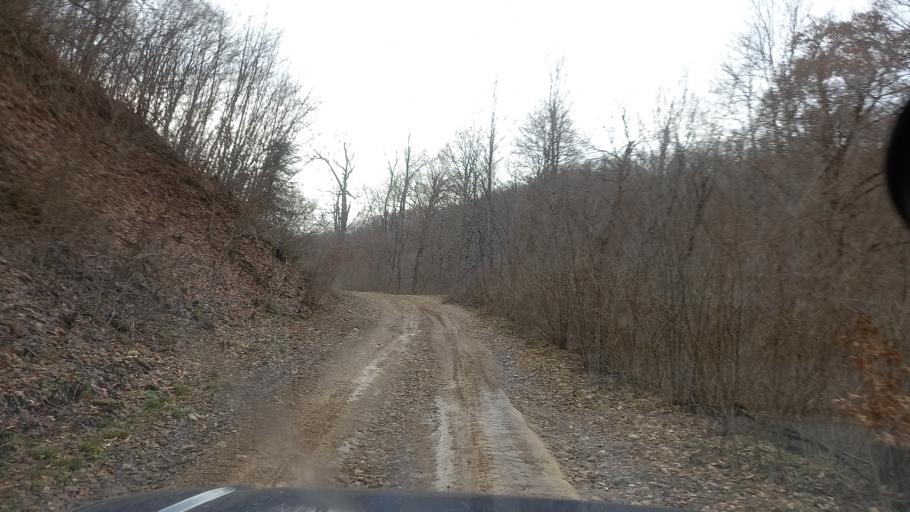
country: RU
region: Adygeya
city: Kamennomostskiy
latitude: 44.1719
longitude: 40.2988
